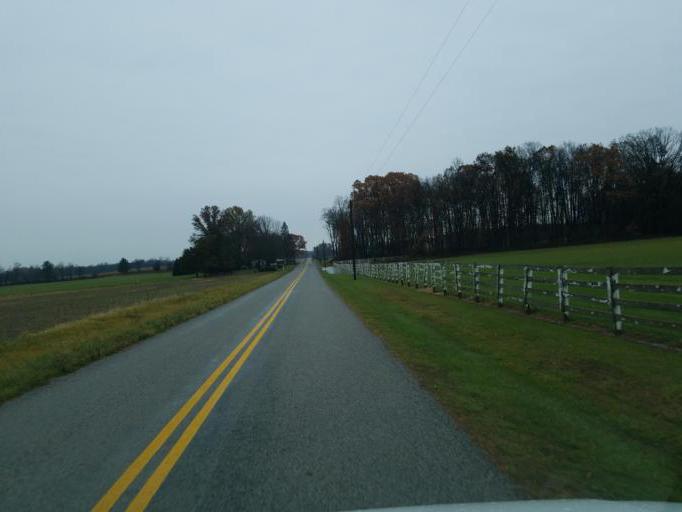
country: US
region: Ohio
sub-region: Knox County
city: Centerburg
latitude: 40.3351
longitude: -82.7759
